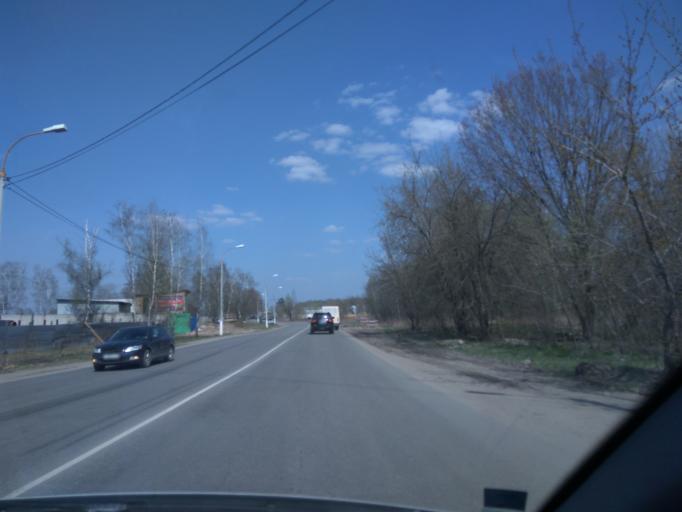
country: RU
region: Moskovskaya
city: Ramenskoye
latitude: 55.5679
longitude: 38.2637
